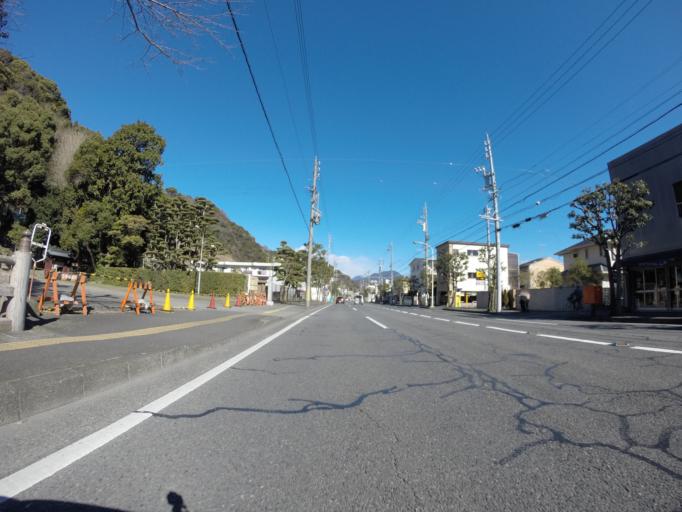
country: JP
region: Shizuoka
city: Shizuoka-shi
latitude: 34.9846
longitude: 138.3764
